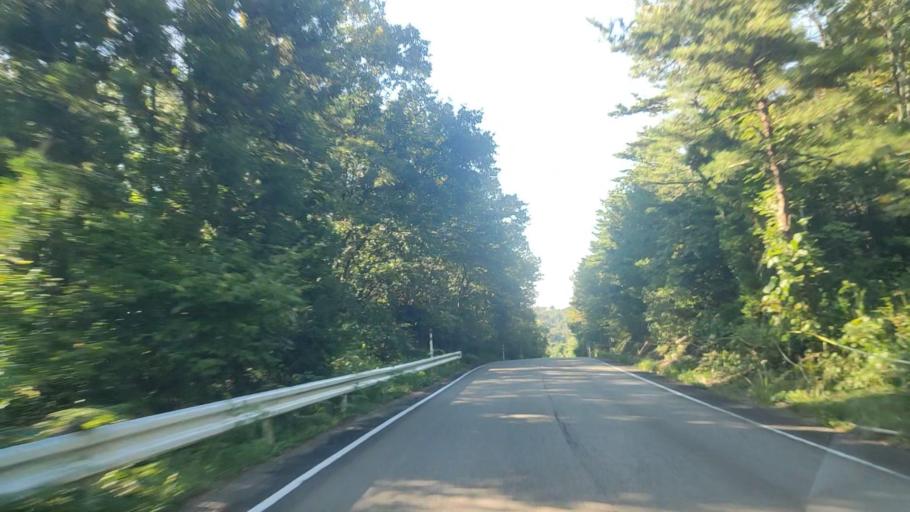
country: JP
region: Ishikawa
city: Nanao
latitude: 37.1178
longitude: 136.9464
